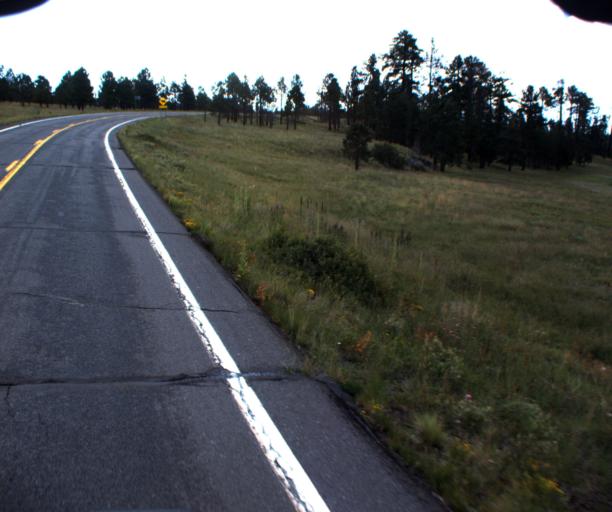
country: US
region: Arizona
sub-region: Apache County
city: Eagar
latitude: 34.0426
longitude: -109.3499
